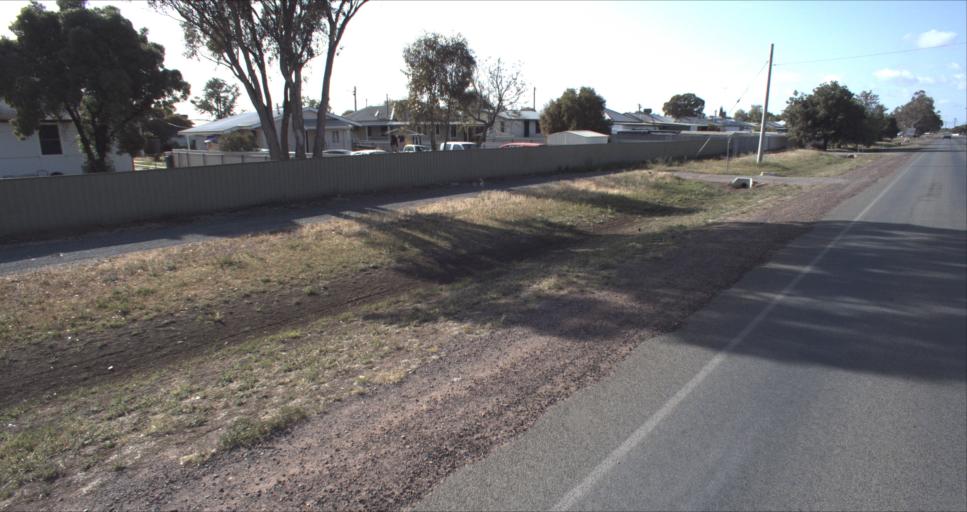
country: AU
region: New South Wales
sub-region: Leeton
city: Leeton
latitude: -34.5645
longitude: 146.3931
